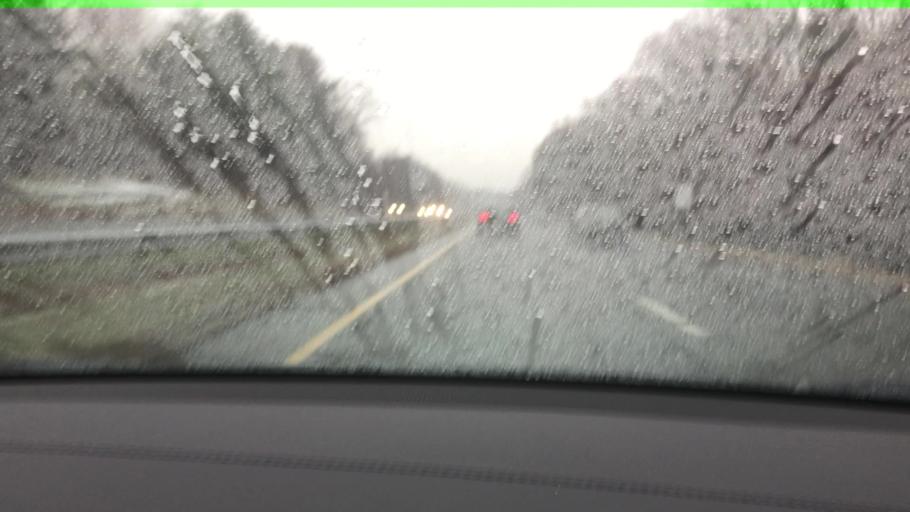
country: US
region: Connecticut
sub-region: New Haven County
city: North Haven
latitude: 41.3909
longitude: -72.8780
